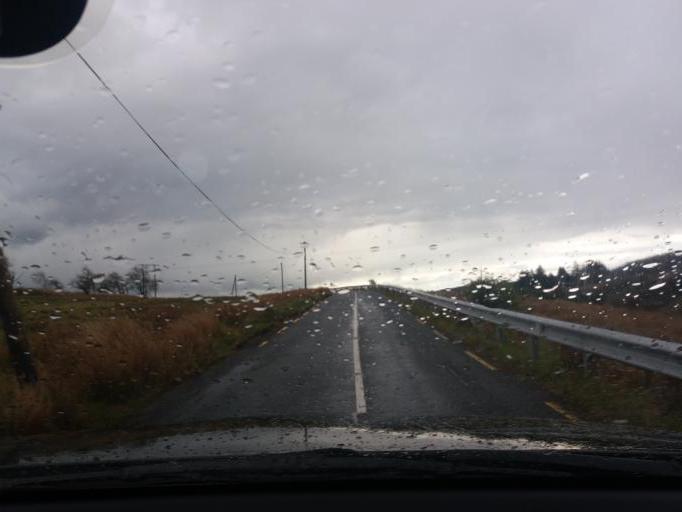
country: IE
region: Ulster
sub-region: An Cabhan
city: Ballyconnell
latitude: 54.1619
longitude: -7.7813
